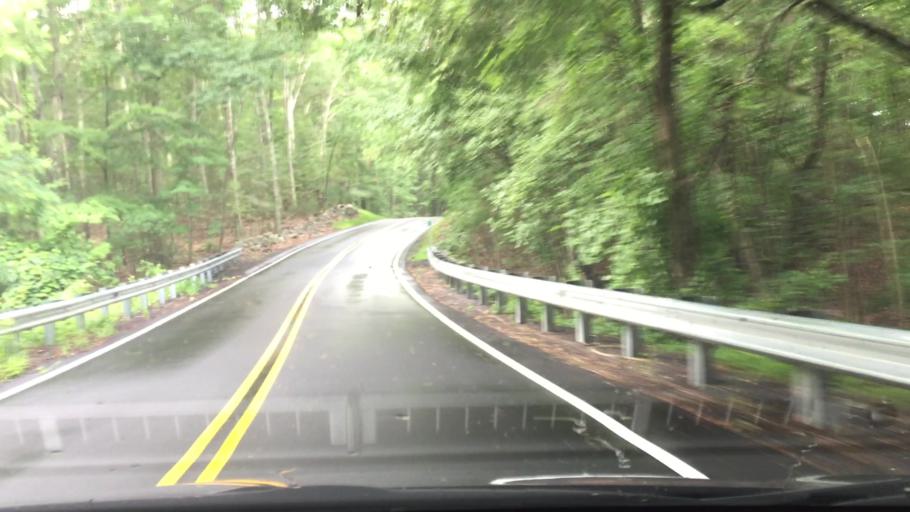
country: US
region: Massachusetts
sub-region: Middlesex County
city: Acton
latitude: 42.5079
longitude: -71.4498
